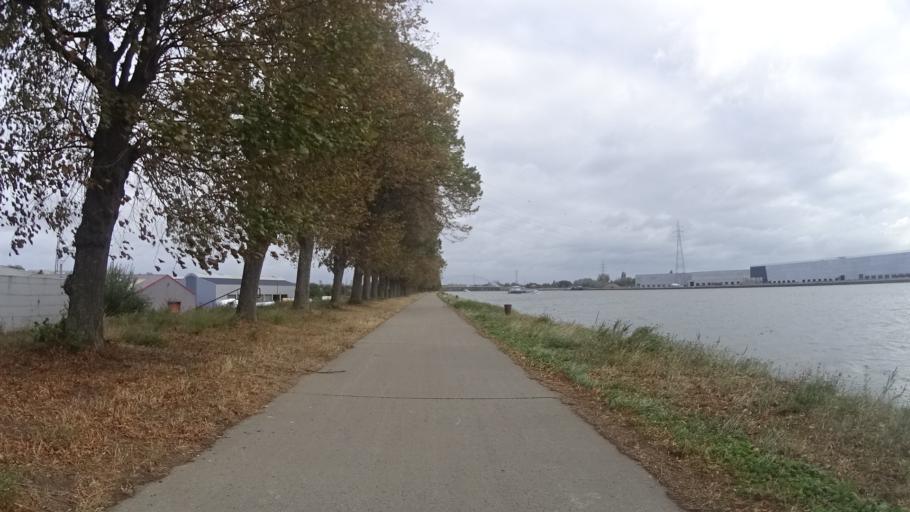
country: BE
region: Wallonia
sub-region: Province de Liege
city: Vise
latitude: 50.7255
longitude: 5.6730
